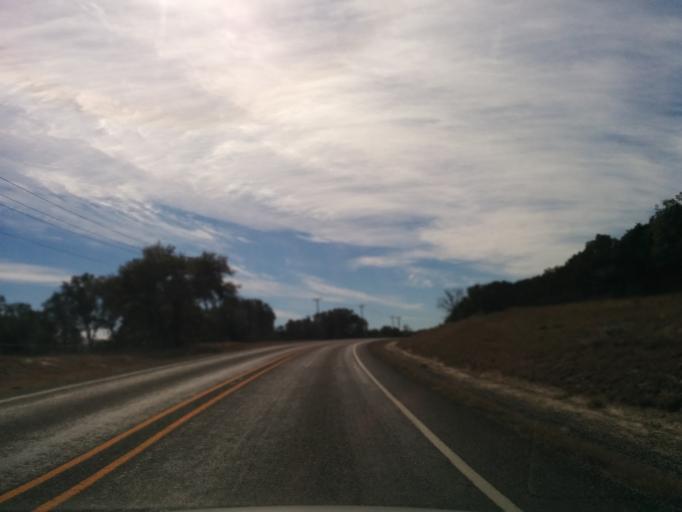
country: US
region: Texas
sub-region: Bexar County
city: Fair Oaks Ranch
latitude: 29.8855
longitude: -98.5564
